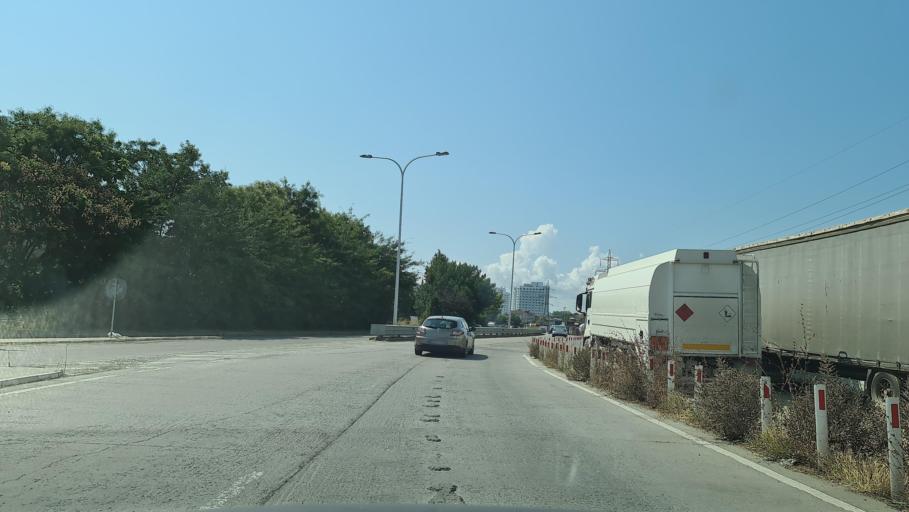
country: RO
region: Constanta
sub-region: Oras Eforie
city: Eforie Nord
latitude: 44.0826
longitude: 28.6397
